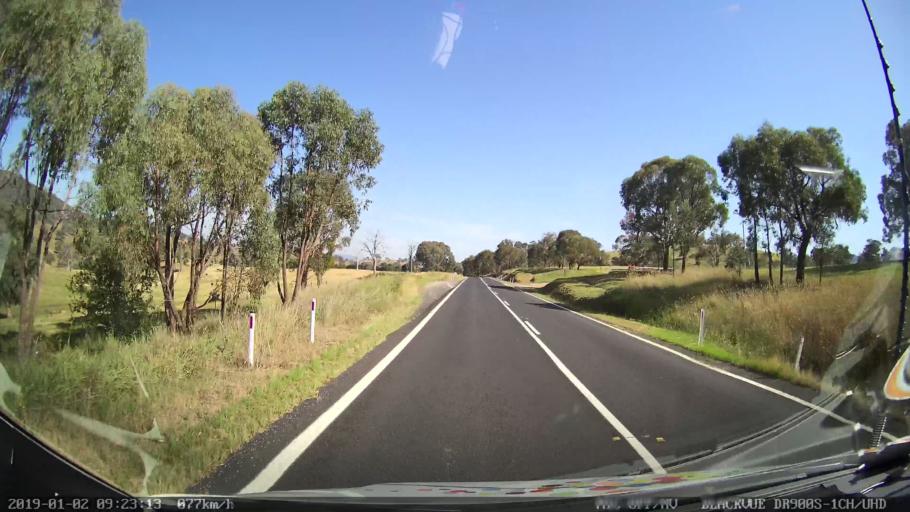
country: AU
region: New South Wales
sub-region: Tumut Shire
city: Tumut
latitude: -35.3900
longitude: 148.2981
